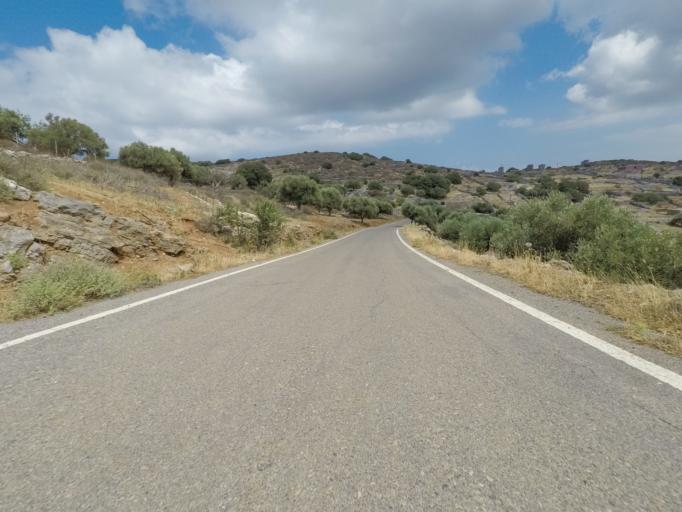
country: GR
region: Crete
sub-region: Nomos Lasithiou
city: Elounda
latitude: 35.2967
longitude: 25.6763
